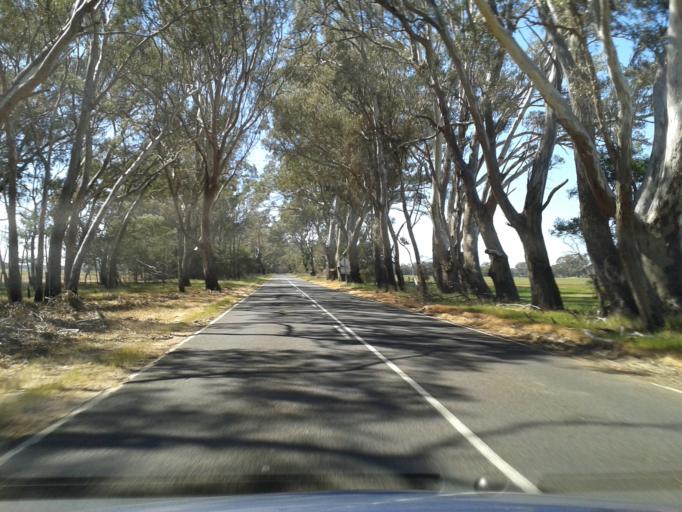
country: AU
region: Victoria
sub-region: Northern Grampians
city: Stawell
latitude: -37.2261
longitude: 142.6643
